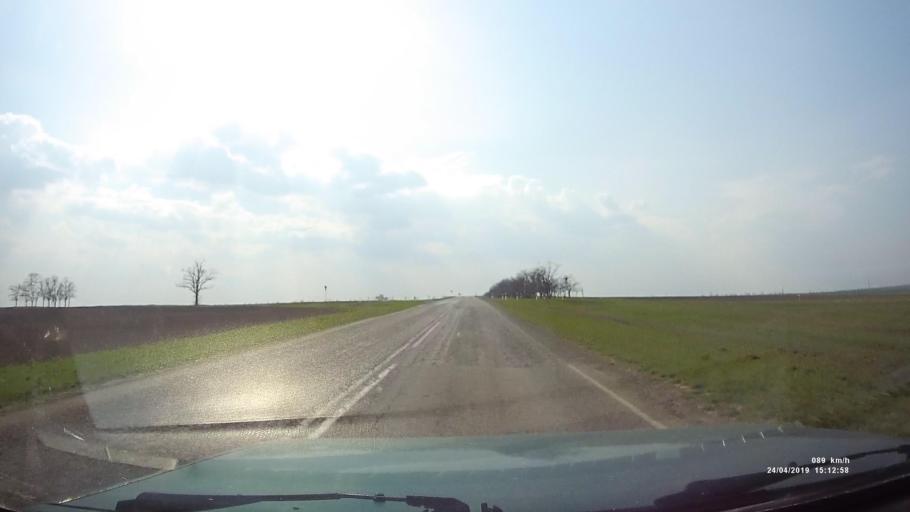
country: RU
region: Rostov
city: Remontnoye
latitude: 46.5464
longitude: 43.2898
